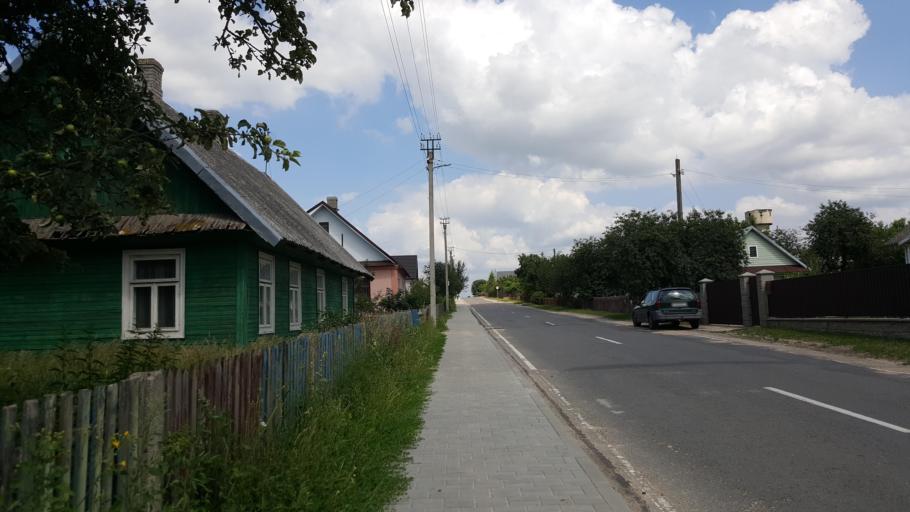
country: BY
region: Brest
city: Kamyanyets
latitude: 52.3998
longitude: 23.8272
